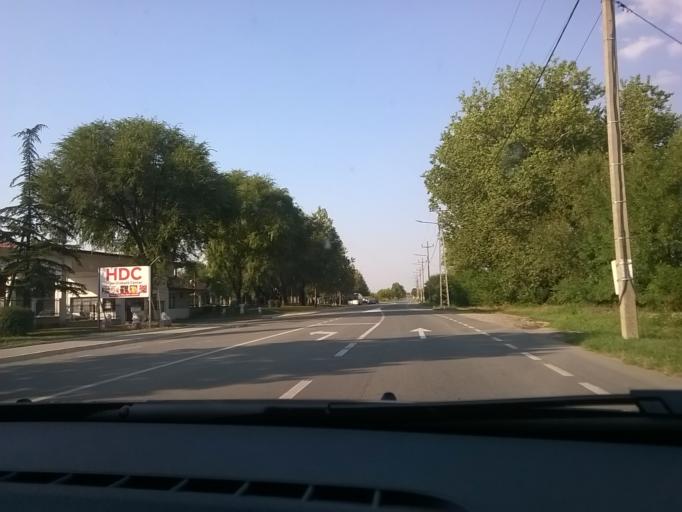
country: RS
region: Autonomna Pokrajina Vojvodina
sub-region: Juznobanatski Okrug
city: Vrsac
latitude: 45.1347
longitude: 21.2870
